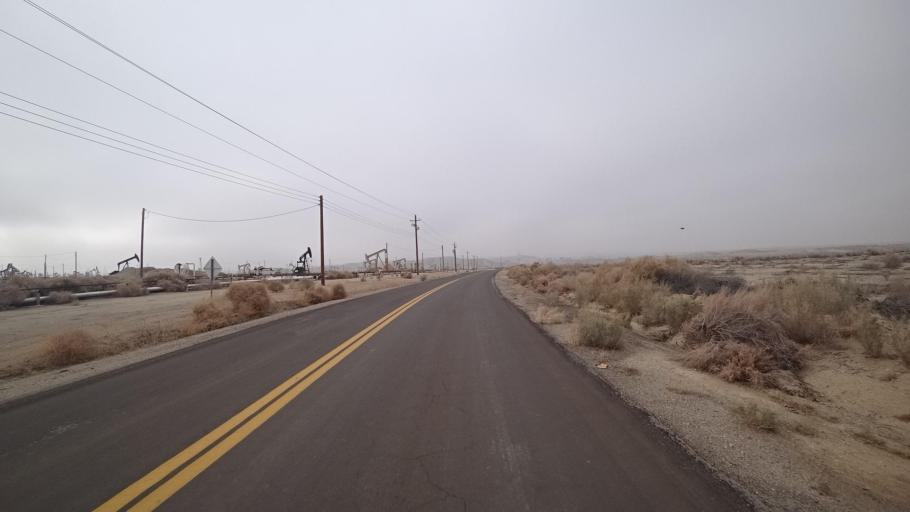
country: US
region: California
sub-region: Kern County
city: Maricopa
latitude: 35.0836
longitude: -119.3882
